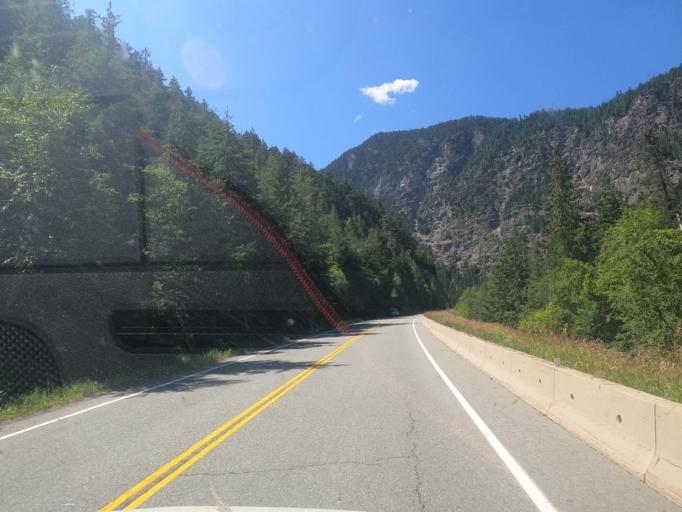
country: CA
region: British Columbia
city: Lillooet
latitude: 50.6455
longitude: -122.0661
